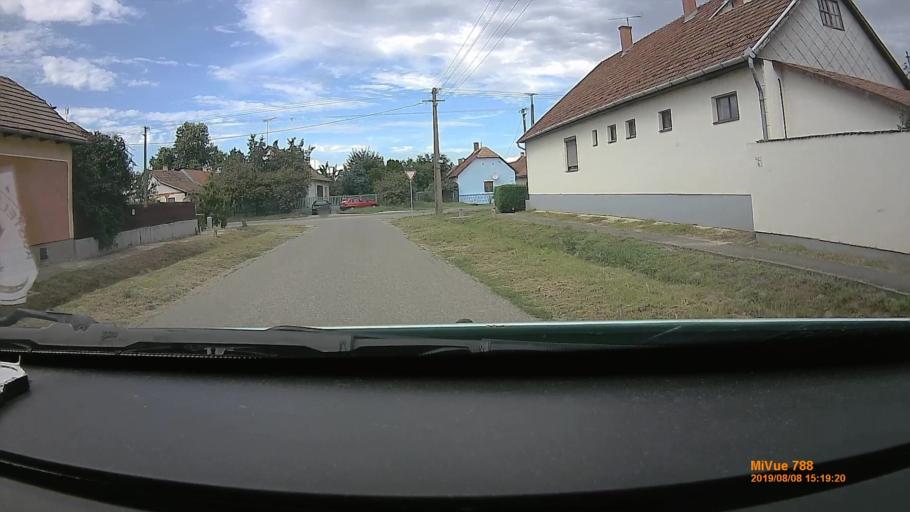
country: HU
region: Szabolcs-Szatmar-Bereg
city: Tunyogmatolcs
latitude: 47.9703
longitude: 22.4587
